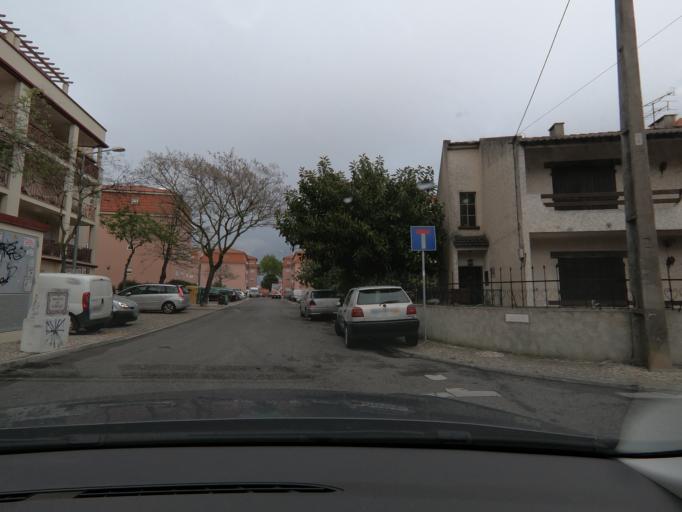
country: PT
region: Lisbon
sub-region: Cascais
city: Sao Domingos de Rana
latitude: 38.7255
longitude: -9.3321
